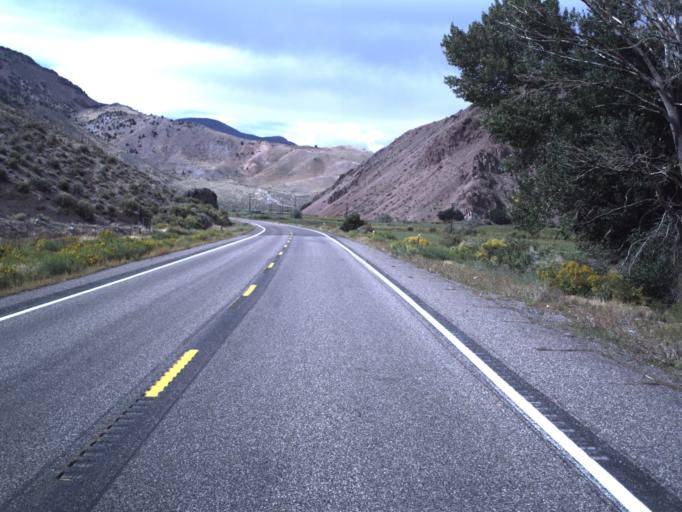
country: US
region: Utah
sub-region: Sevier County
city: Monroe
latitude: 38.4747
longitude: -112.2383
